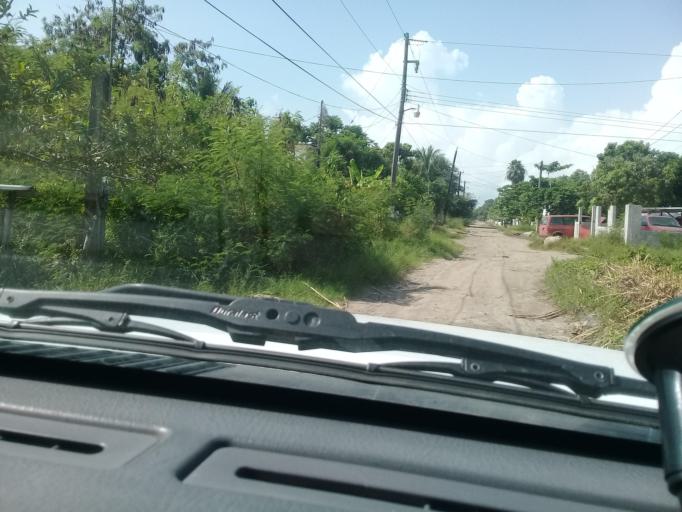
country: MX
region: Veracruz
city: Moralillo
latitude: 22.2298
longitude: -97.9033
